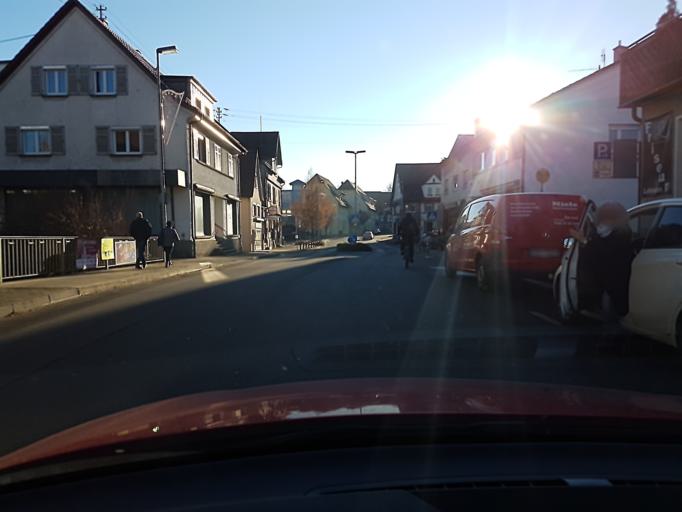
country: DE
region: Baden-Wuerttemberg
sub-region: Karlsruhe Region
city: Illingen
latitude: 48.9554
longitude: 8.9190
